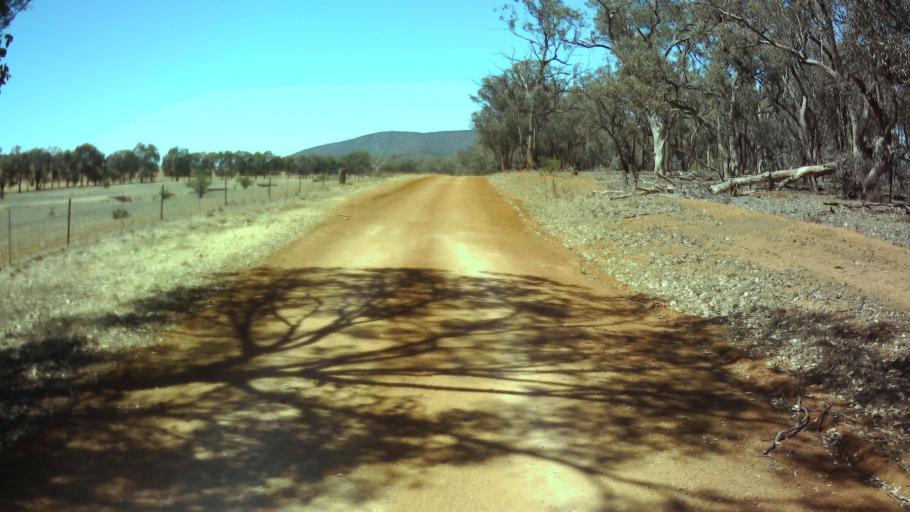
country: AU
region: New South Wales
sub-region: Weddin
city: Grenfell
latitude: -33.9504
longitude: 148.0845
